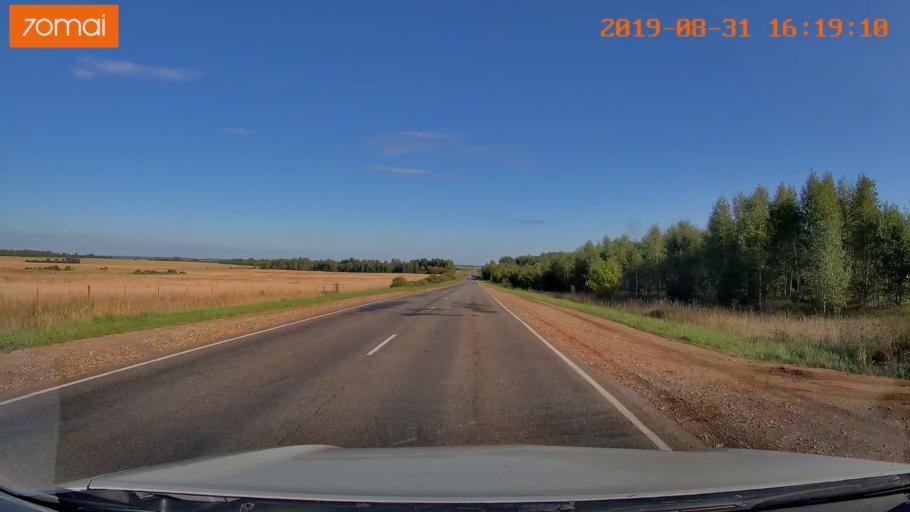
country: RU
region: Kaluga
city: Nikola-Lenivets
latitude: 54.5311
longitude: 35.5720
